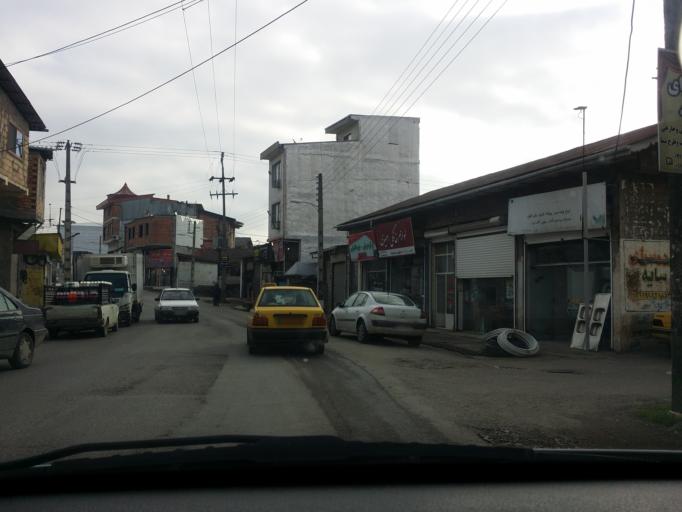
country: IR
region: Mazandaran
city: Chalus
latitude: 36.6581
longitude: 51.4094
